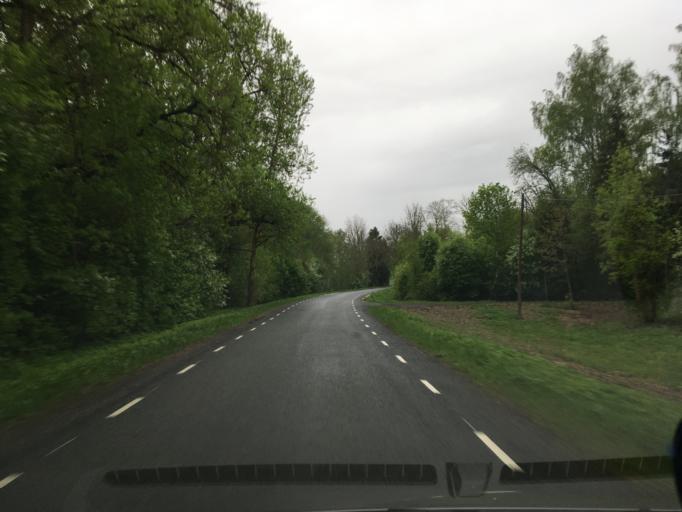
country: EE
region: Harju
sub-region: Keila linn
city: Keila
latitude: 59.2345
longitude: 24.4834
